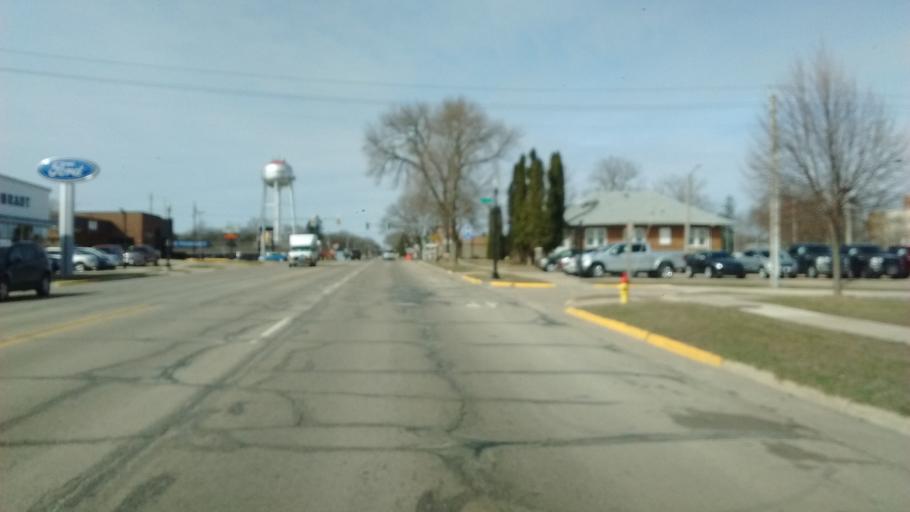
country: US
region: Iowa
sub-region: Bremer County
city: Waverly
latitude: 42.7257
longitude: -92.4815
